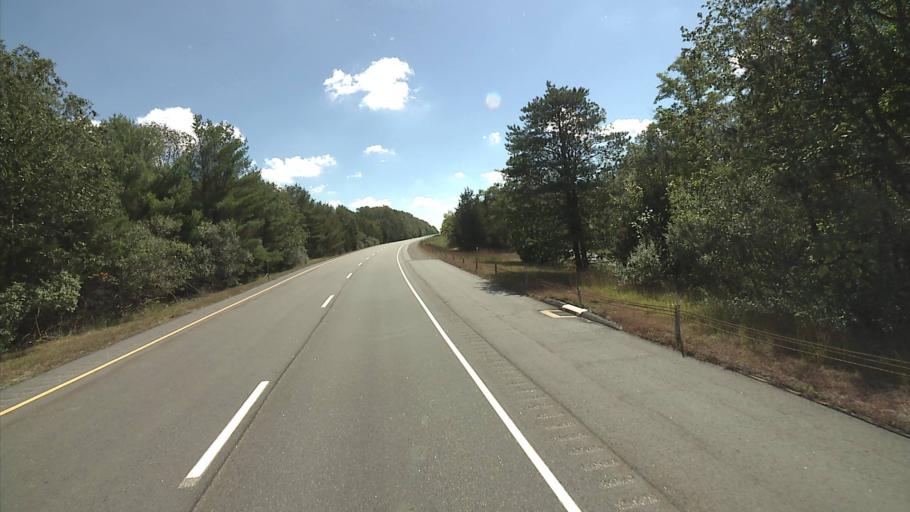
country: US
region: Connecticut
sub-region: New London County
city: Colchester
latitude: 41.5579
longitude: -72.3222
